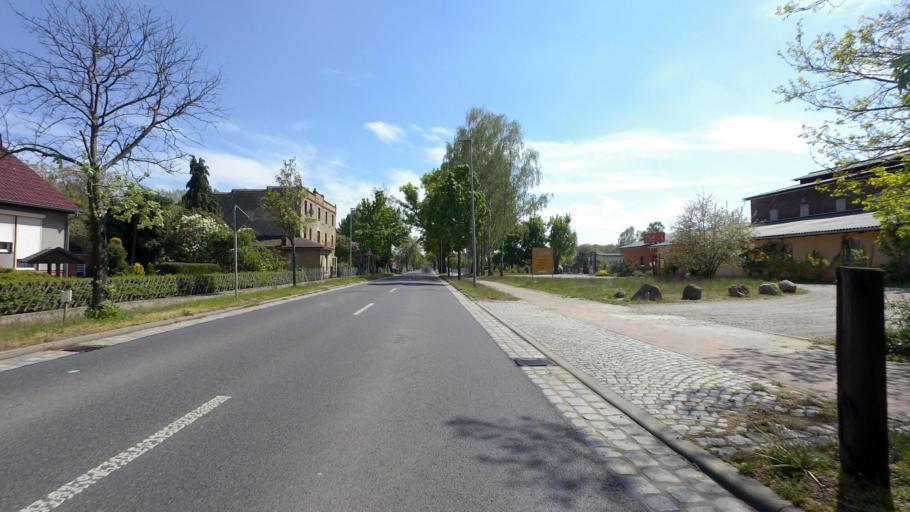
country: DE
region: Brandenburg
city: Tschernitz
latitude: 51.6058
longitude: 14.6094
